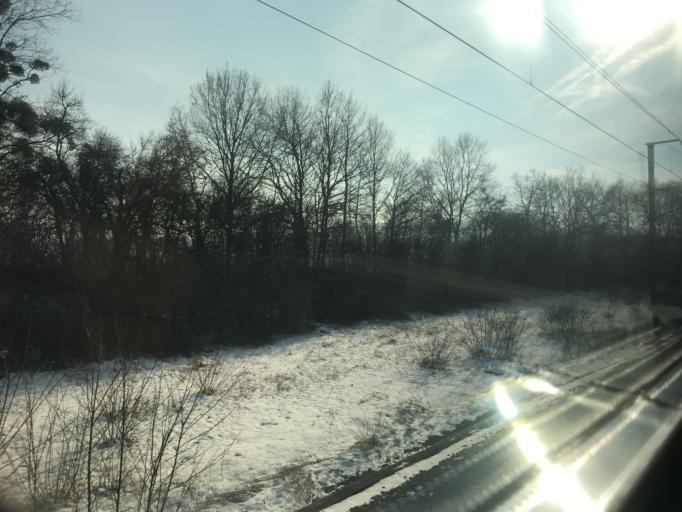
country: LU
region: Luxembourg
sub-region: Canton de Luxembourg
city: Niederanven
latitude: 49.6551
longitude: 6.2978
